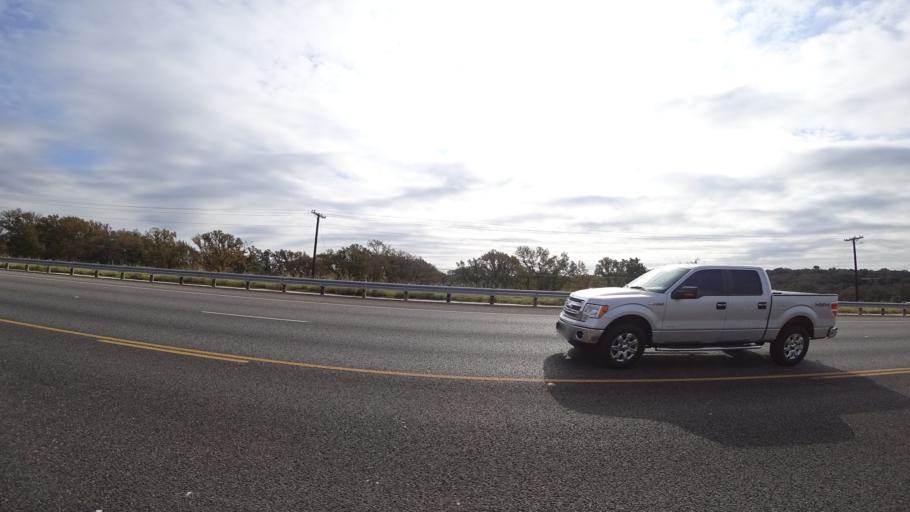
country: US
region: Texas
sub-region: Travis County
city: Manchaca
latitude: 30.1281
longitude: -97.8594
